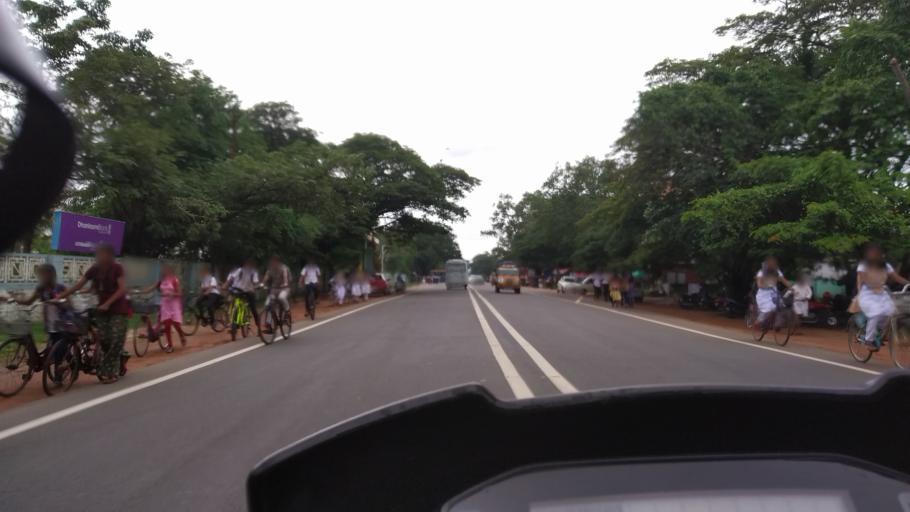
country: IN
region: Kerala
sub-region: Alappuzha
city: Shertallai
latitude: 9.6211
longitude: 76.3317
